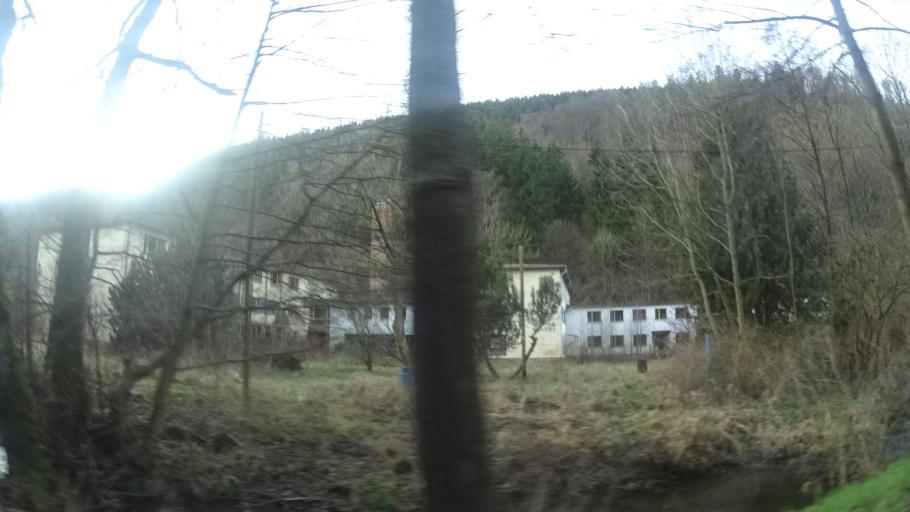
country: DE
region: Thuringia
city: Rohrbach
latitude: 50.6163
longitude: 11.2139
